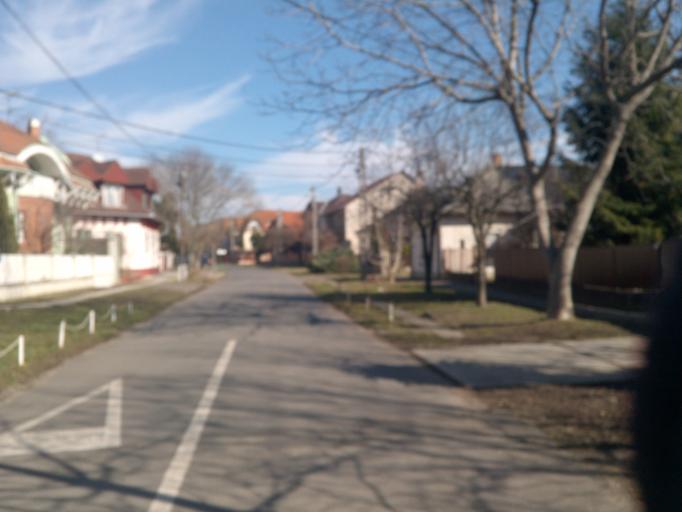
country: HU
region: Hajdu-Bihar
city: Hajduszoboszlo
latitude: 47.4445
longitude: 21.3982
